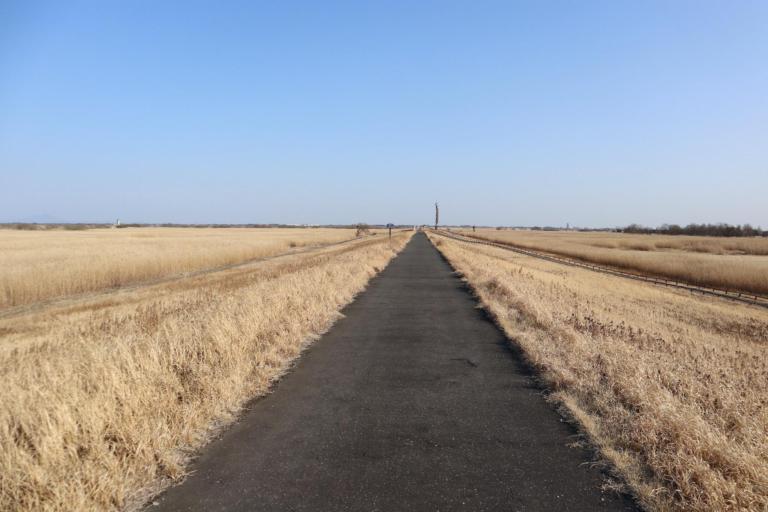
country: JP
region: Tochigi
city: Fujioka
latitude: 36.2581
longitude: 139.6597
